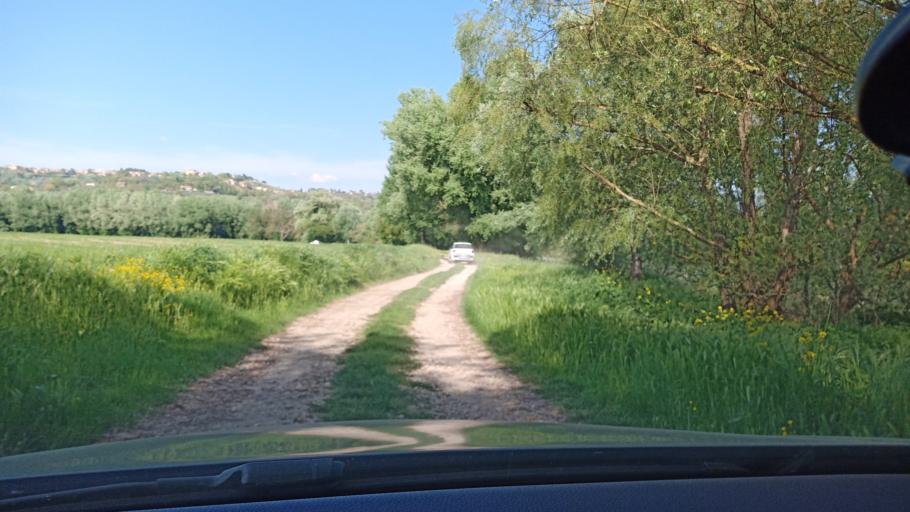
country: IT
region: Latium
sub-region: Provincia di Rieti
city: Forano
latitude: 42.2792
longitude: 12.5822
